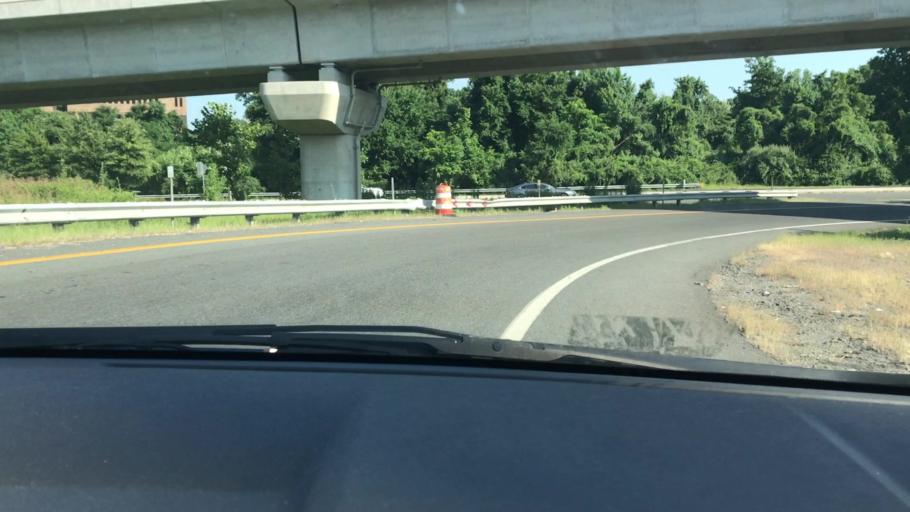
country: US
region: Virginia
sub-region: Fairfax County
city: Pimmit Hills
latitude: 38.9232
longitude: -77.2141
